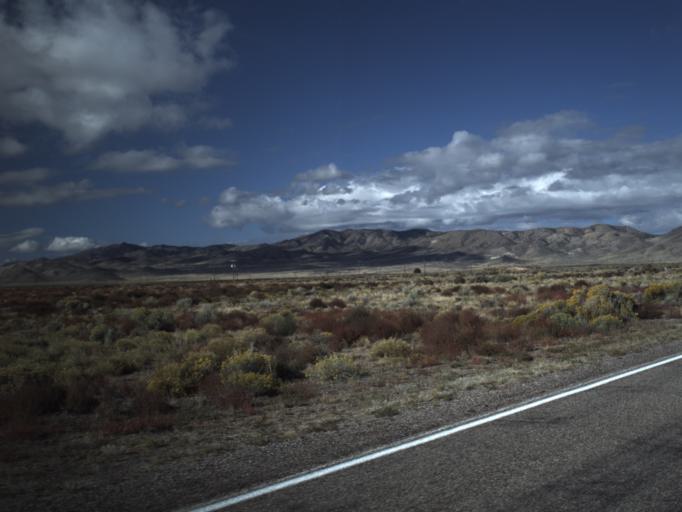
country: US
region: Utah
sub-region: Beaver County
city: Milford
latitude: 38.3987
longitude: -113.0293
